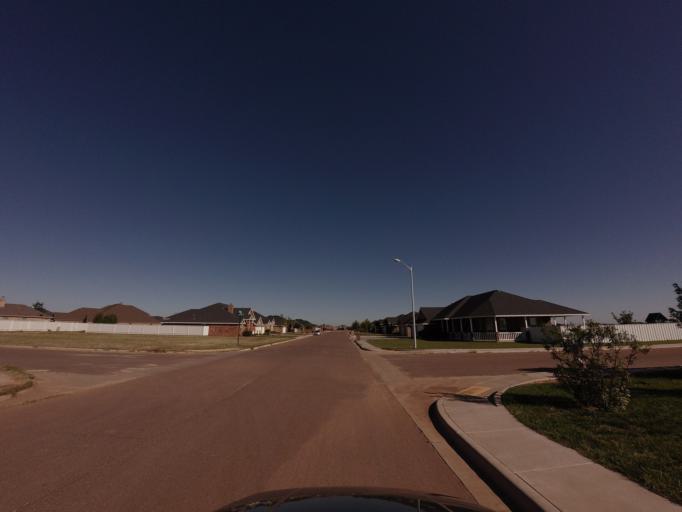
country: US
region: New Mexico
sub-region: Curry County
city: Clovis
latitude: 34.4390
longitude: -103.1703
